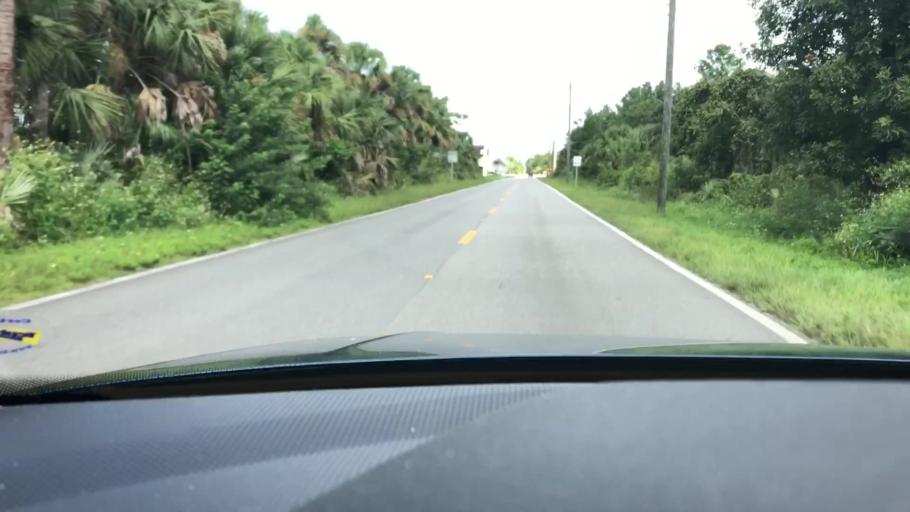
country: US
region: Florida
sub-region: Volusia County
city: Edgewater
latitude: 28.9479
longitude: -80.9442
